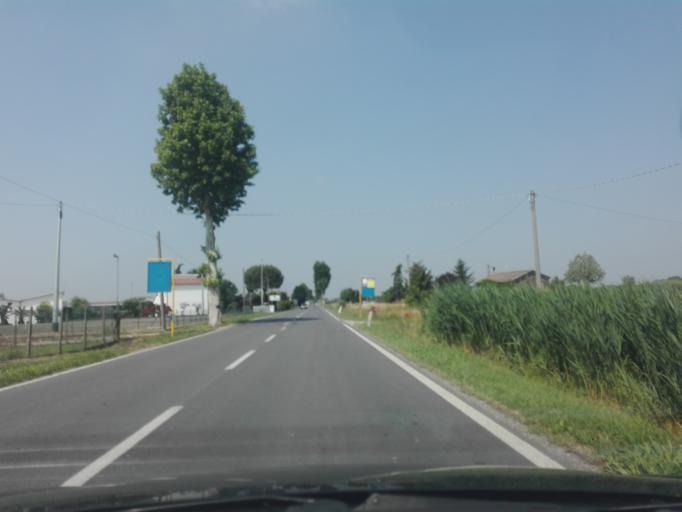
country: IT
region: Veneto
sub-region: Provincia di Rovigo
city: Villadose
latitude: 45.0645
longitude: 11.9188
